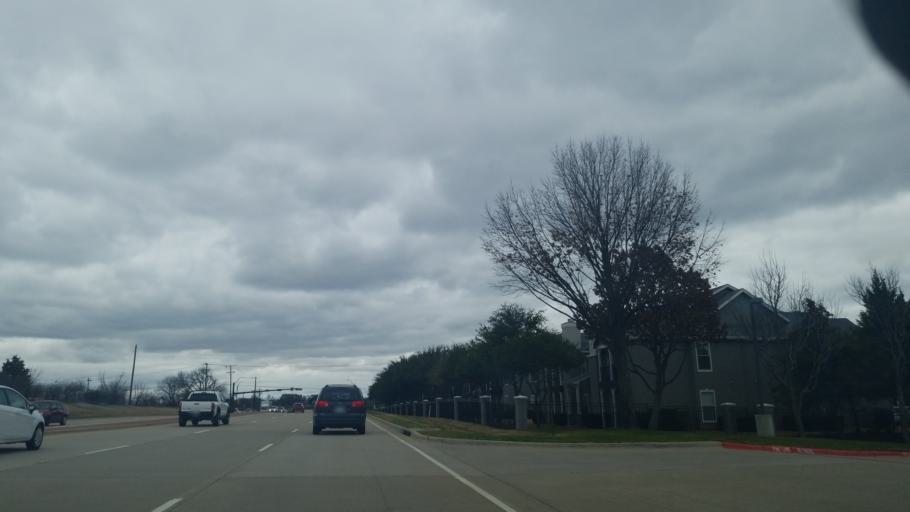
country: US
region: Texas
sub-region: Denton County
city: Double Oak
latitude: 33.0569
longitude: -97.0754
